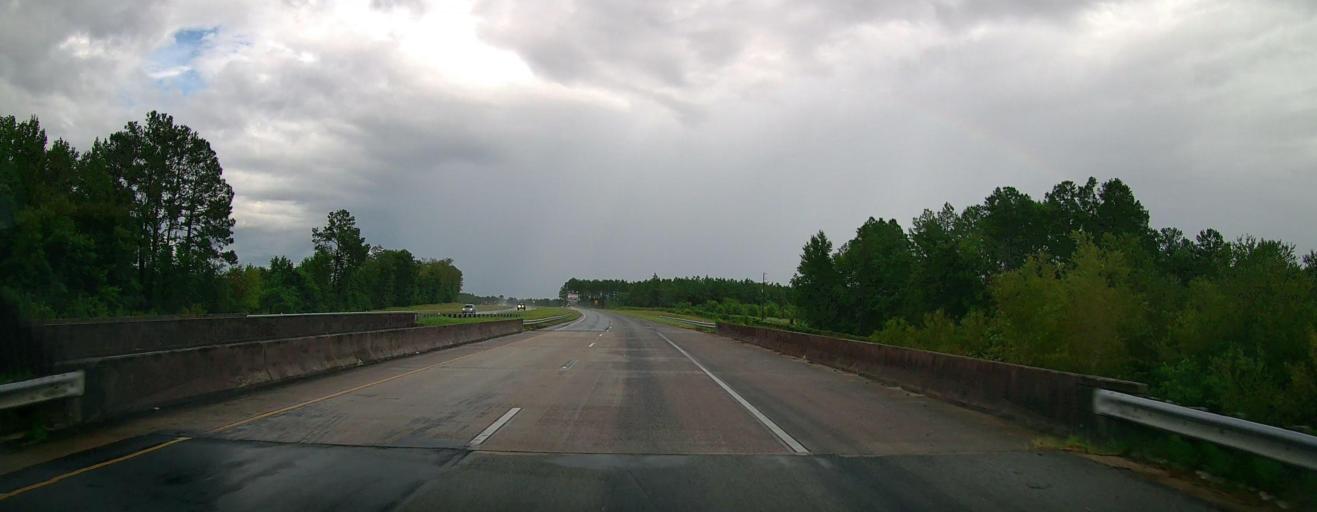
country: US
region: Georgia
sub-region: Ware County
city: Deenwood
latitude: 31.2541
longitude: -82.4762
